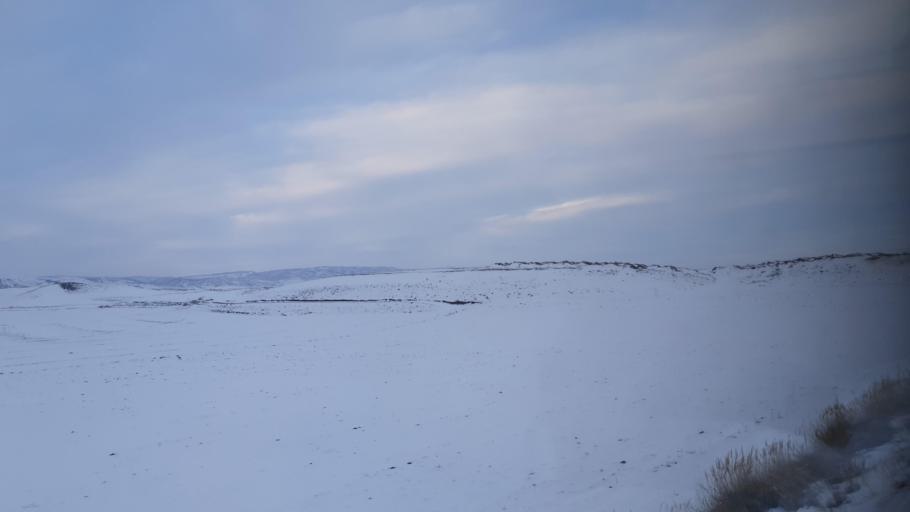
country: TR
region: Yozgat
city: Yerkoy
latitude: 39.6859
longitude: 34.4157
